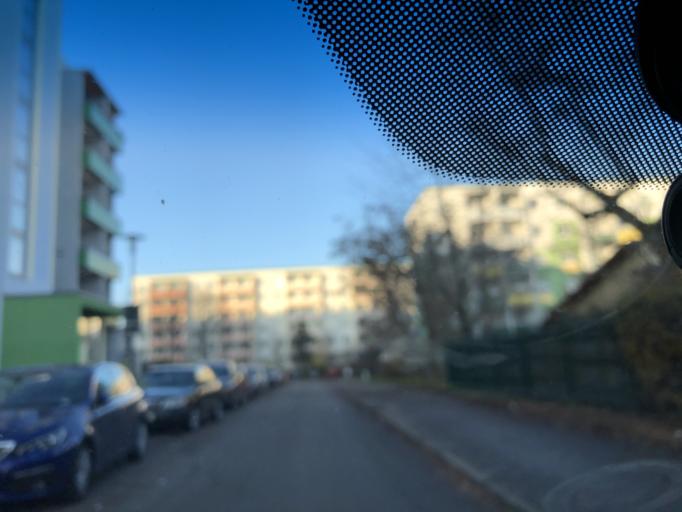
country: DE
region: Saxony-Anhalt
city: Halle Neustadt
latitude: 51.4802
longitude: 11.9074
